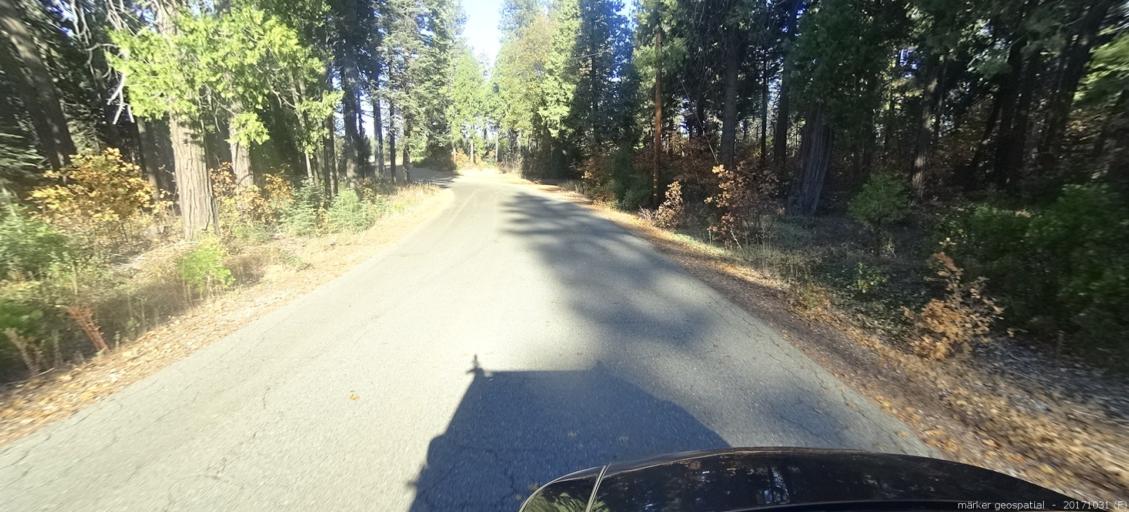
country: US
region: California
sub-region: Shasta County
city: Shingletown
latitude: 40.5176
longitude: -121.8171
